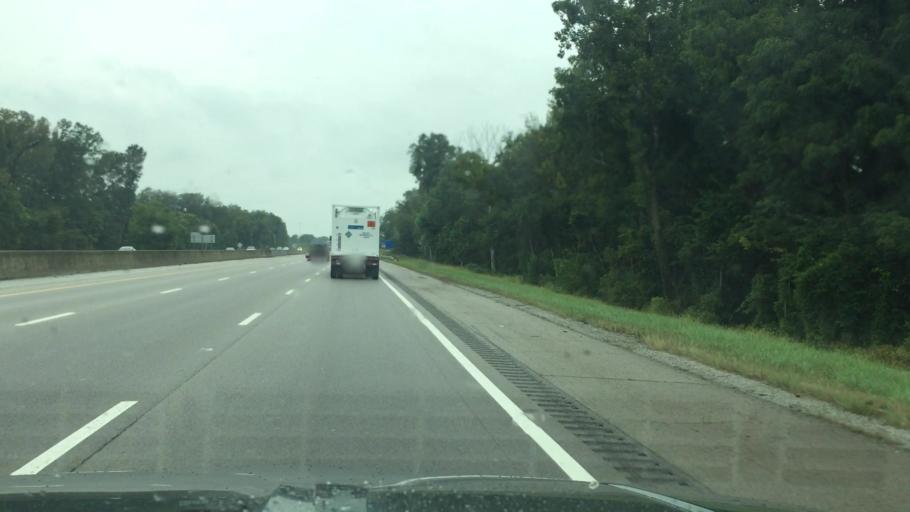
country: US
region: Ohio
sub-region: Clark County
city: Crystal Lakes
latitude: 39.8647
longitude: -84.0206
